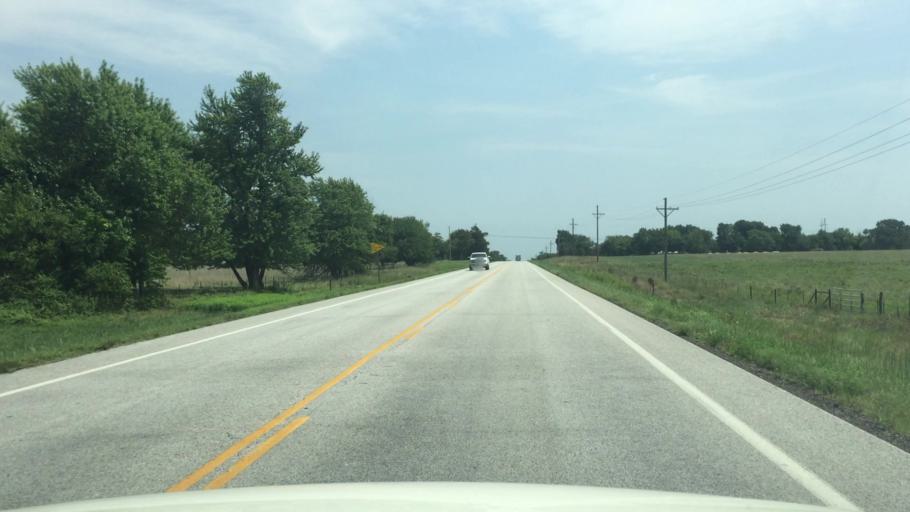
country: US
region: Kansas
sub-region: Cherokee County
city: Columbus
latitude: 37.1780
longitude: -94.7868
